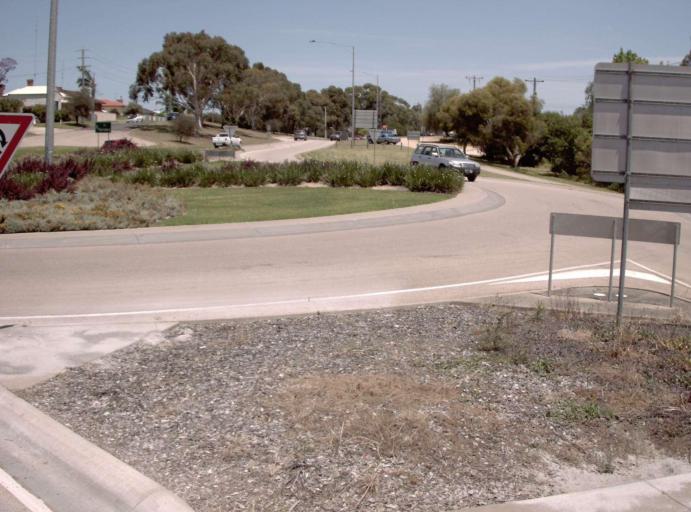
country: AU
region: Victoria
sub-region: East Gippsland
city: Bairnsdale
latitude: -37.8186
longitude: 147.6493
